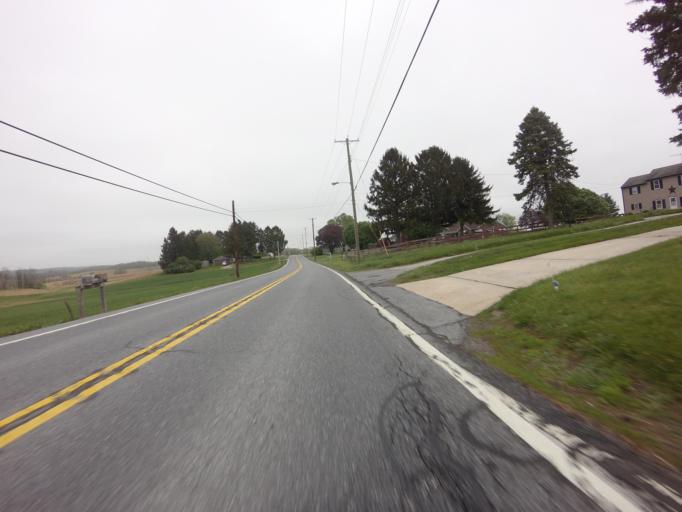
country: US
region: Maryland
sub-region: Baltimore County
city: Hunt Valley
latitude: 39.5840
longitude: -76.7155
